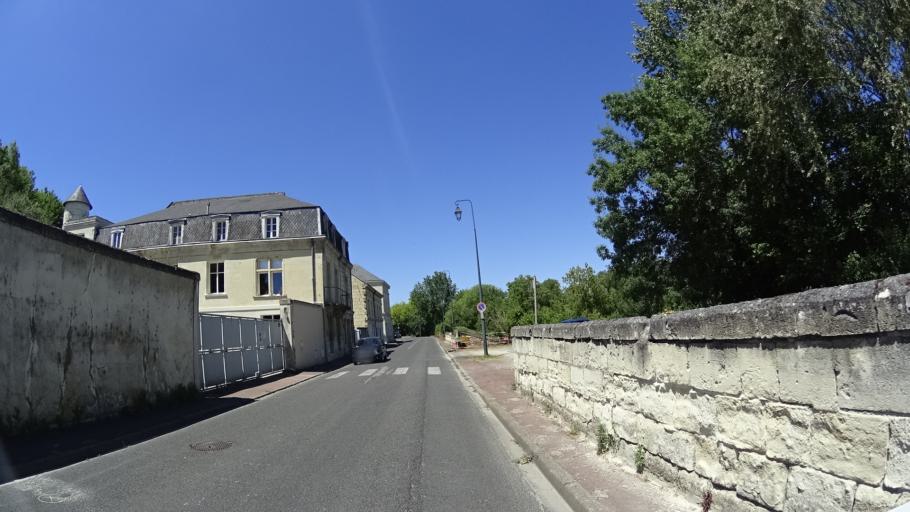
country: FR
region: Pays de la Loire
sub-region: Departement de Maine-et-Loire
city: Saumur
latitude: 47.2731
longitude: -0.1073
